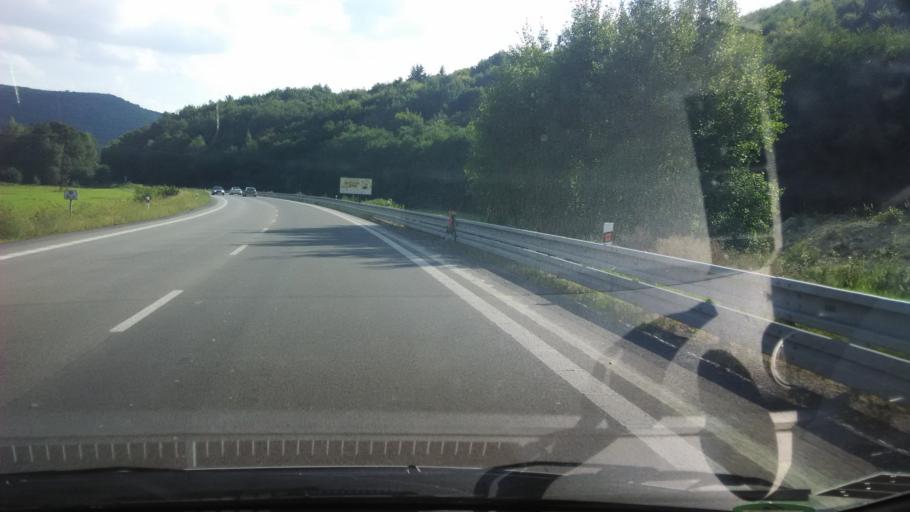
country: SK
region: Banskobystricky
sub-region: Okres Ziar nad Hronom
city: Kremnica
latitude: 48.6390
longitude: 18.9013
